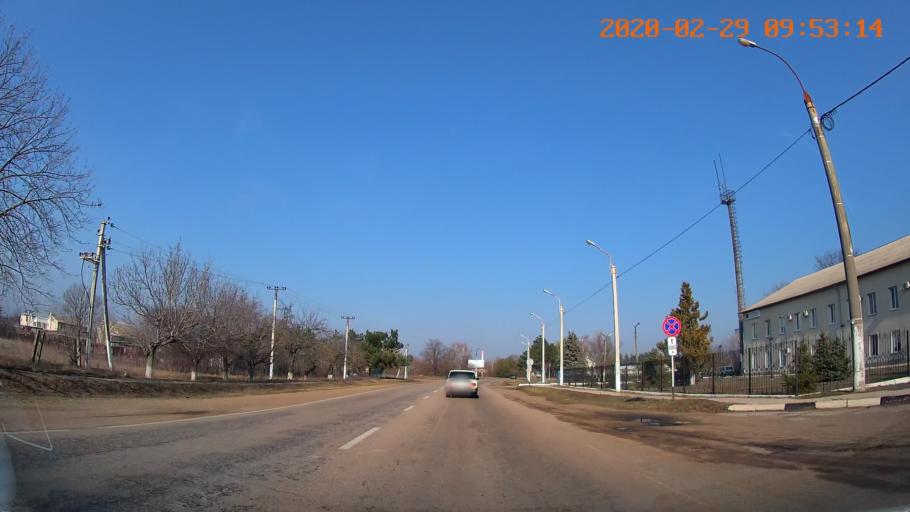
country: MD
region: Telenesti
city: Slobozia
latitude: 46.7208
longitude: 29.7231
